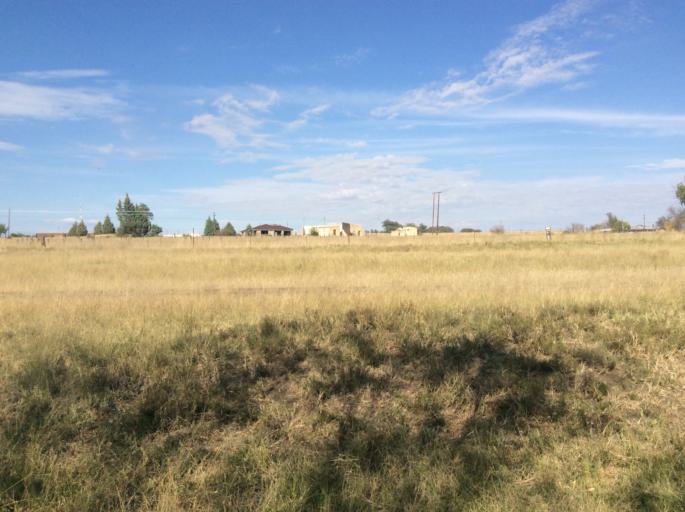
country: LS
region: Mafeteng
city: Mafeteng
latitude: -29.7327
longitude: 27.0287
